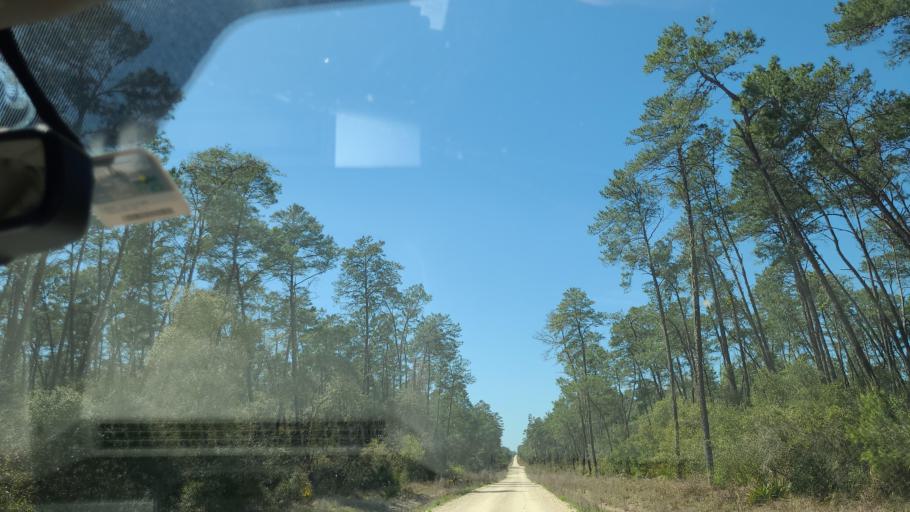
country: US
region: Florida
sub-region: Putnam County
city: Interlachen
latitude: 29.4283
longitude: -81.8855
